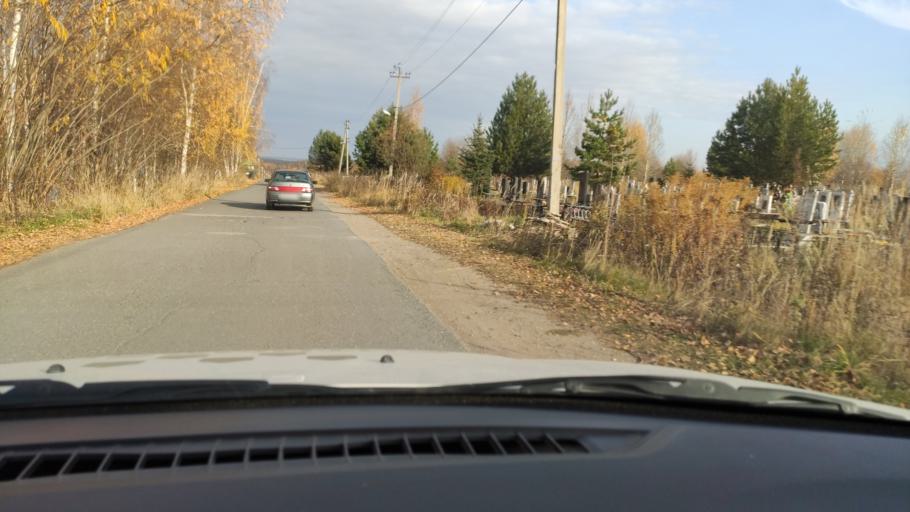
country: RU
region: Perm
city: Kondratovo
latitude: 58.0642
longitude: 56.1437
